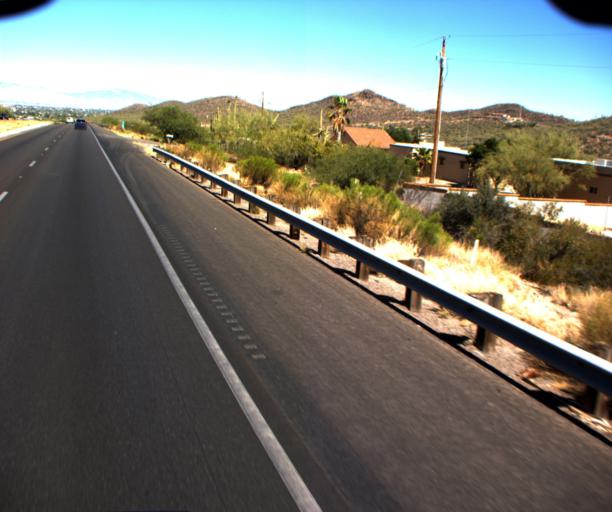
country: US
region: Arizona
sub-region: Pima County
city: Drexel Heights
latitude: 32.1765
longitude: -111.0273
